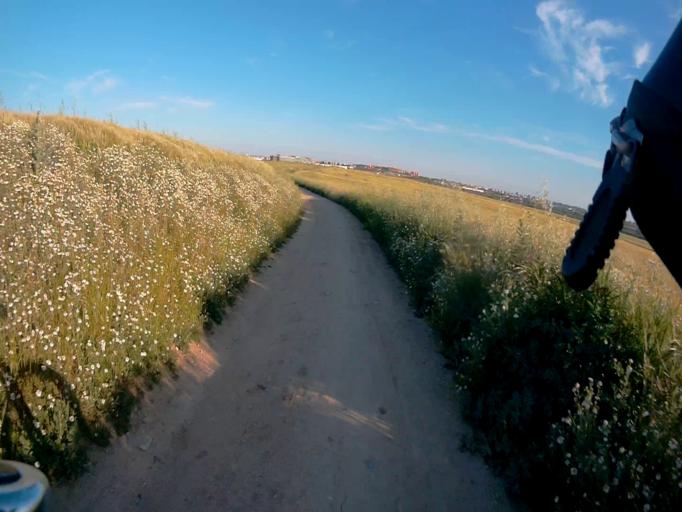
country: ES
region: Madrid
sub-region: Provincia de Madrid
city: Alcorcon
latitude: 40.3208
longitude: -3.8130
